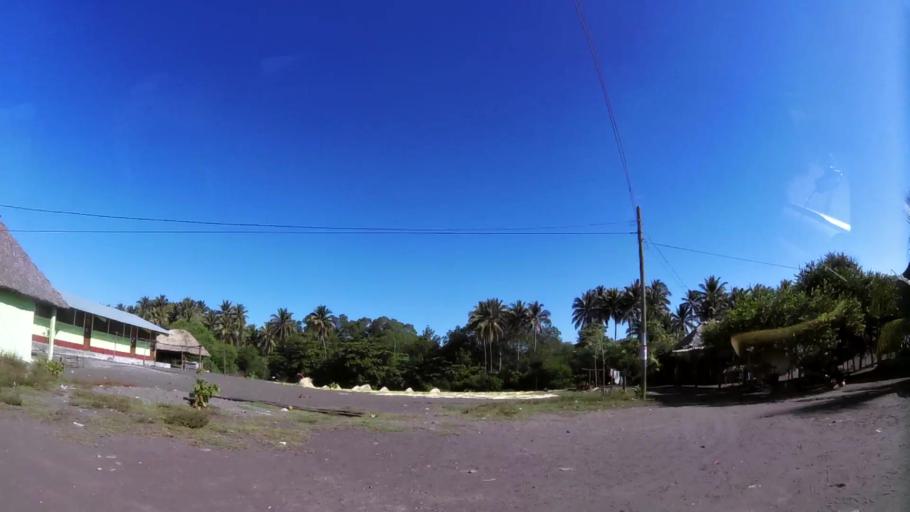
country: GT
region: Jutiapa
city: Pasaco
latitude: 13.8554
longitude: -90.3866
